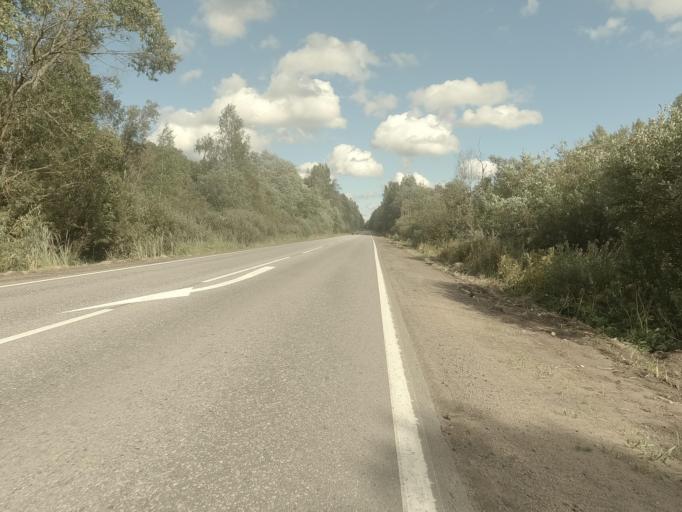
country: RU
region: Leningrad
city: Romanovka
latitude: 60.0236
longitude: 30.7073
